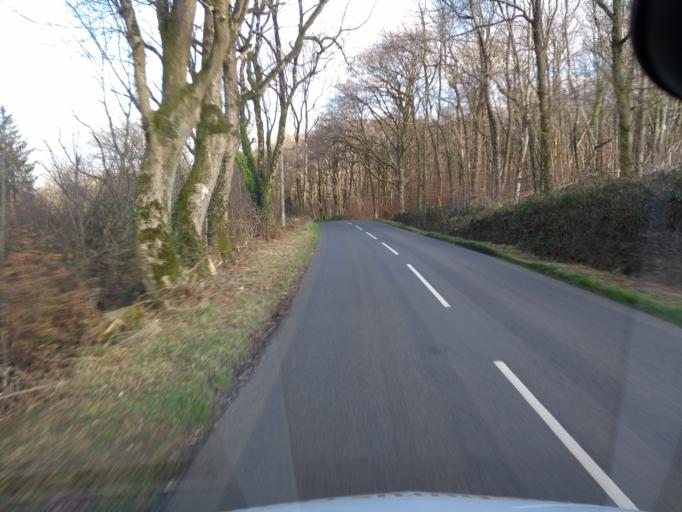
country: GB
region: England
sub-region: Somerset
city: Creech Saint Michael
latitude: 50.9398
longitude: -3.0431
